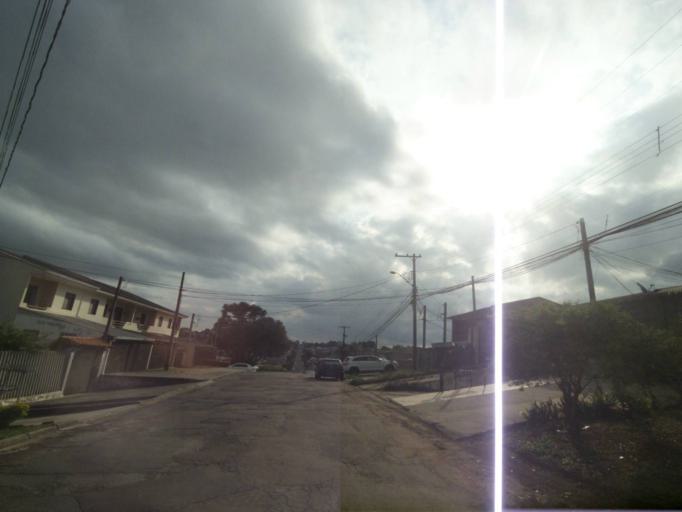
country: BR
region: Parana
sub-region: Pinhais
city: Pinhais
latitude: -25.4061
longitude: -49.2017
